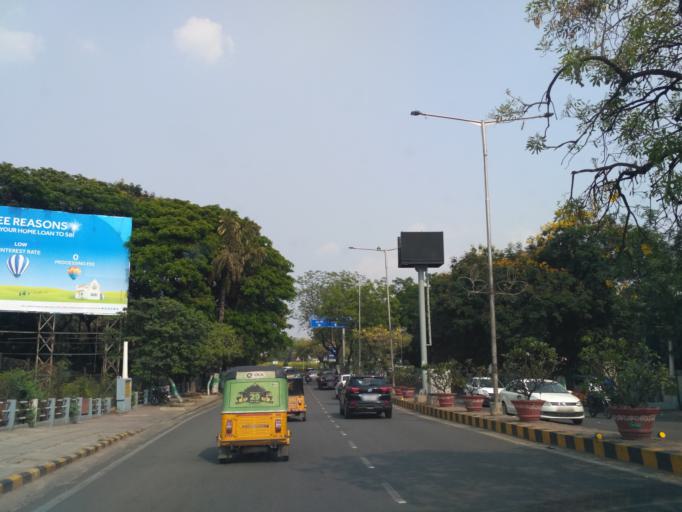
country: IN
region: Telangana
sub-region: Hyderabad
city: Hyderabad
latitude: 17.4153
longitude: 78.4643
